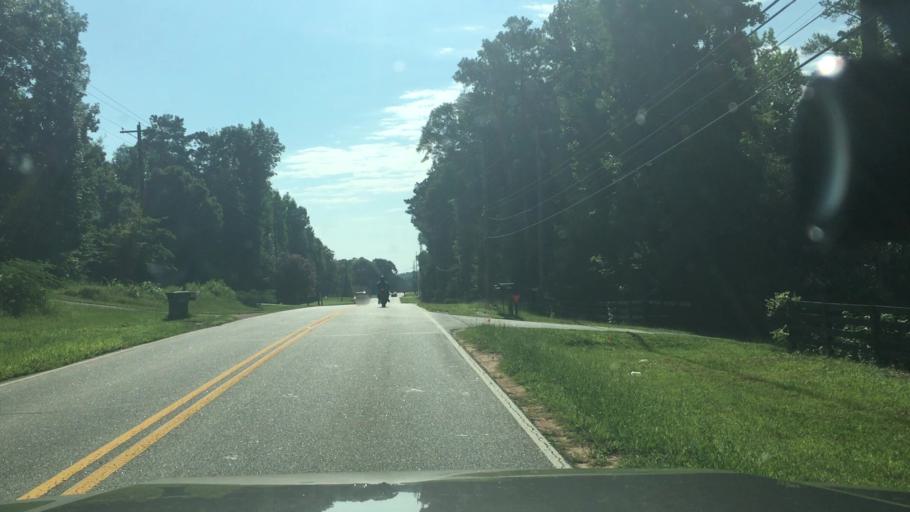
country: US
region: Georgia
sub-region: Coweta County
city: East Newnan
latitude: 33.3559
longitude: -84.7193
